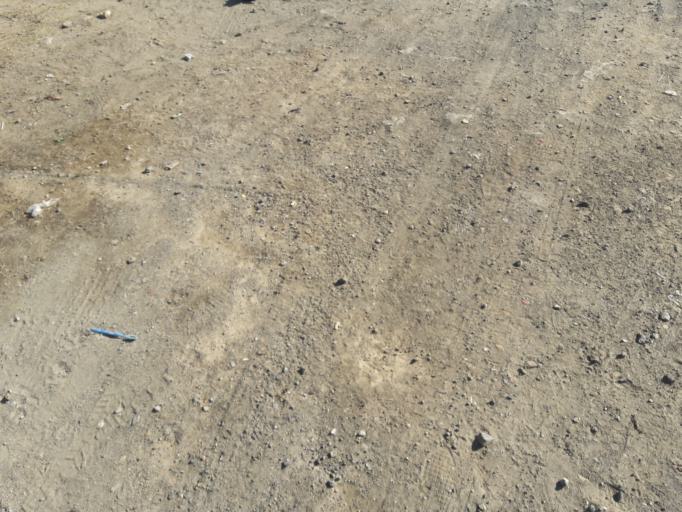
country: GT
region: Guatemala
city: Amatitlan
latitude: 14.4751
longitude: -90.6211
